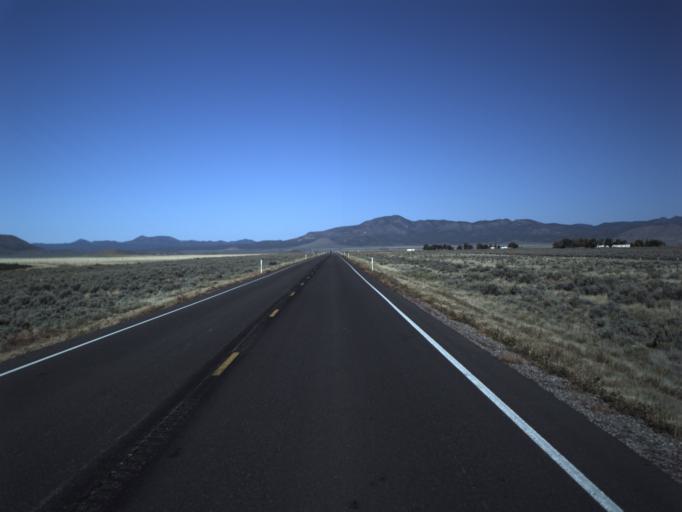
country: US
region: Utah
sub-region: Washington County
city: Enterprise
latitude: 37.7618
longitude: -113.8038
